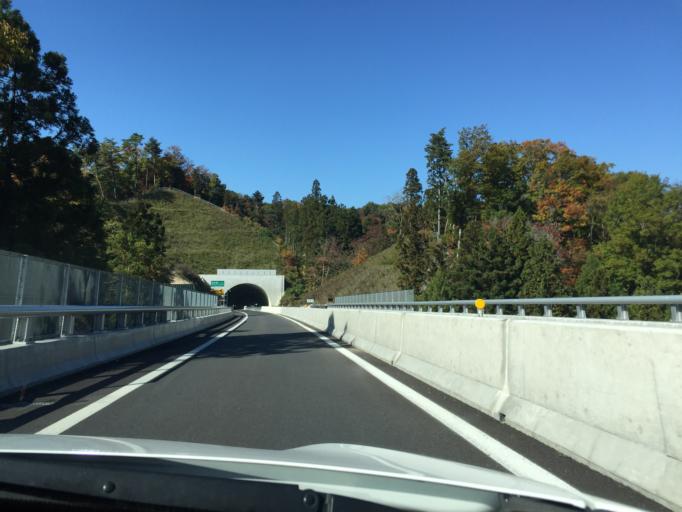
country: JP
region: Fukushima
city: Yanagawamachi-saiwaicho
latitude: 37.7537
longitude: 140.6602
